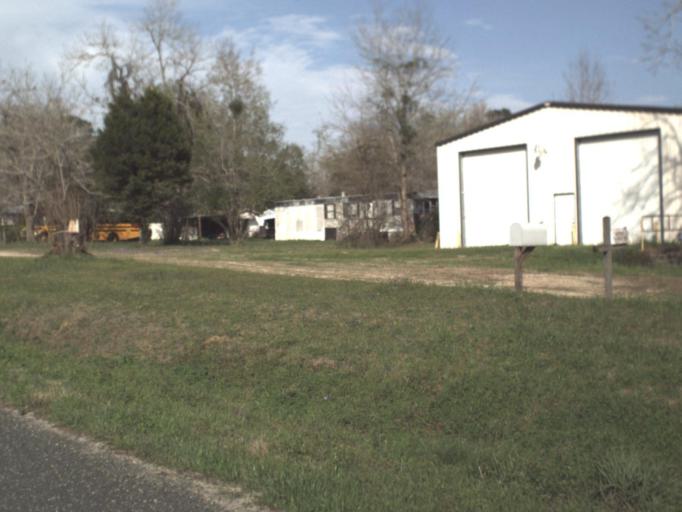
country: US
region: Florida
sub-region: Jefferson County
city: Monticello
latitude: 30.5039
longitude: -83.8782
